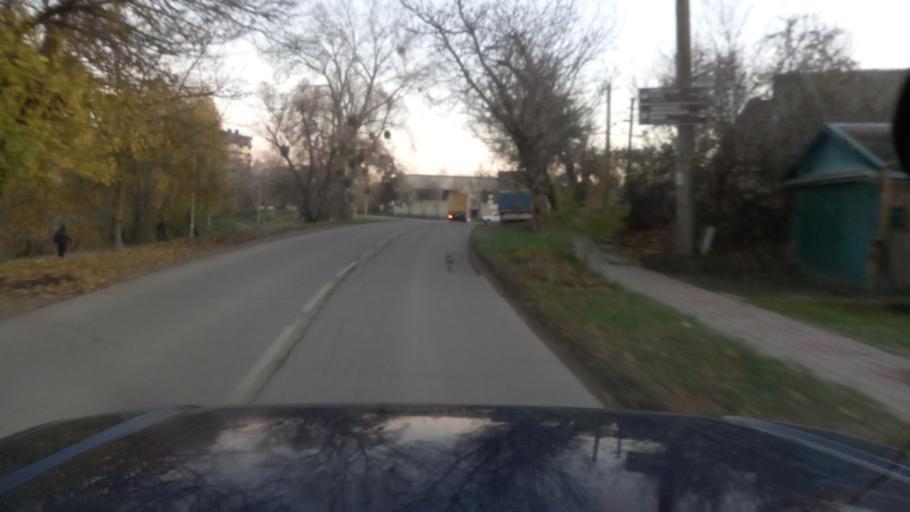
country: RU
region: Krasnodarskiy
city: Goryachiy Klyuch
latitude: 44.6332
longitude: 39.1184
